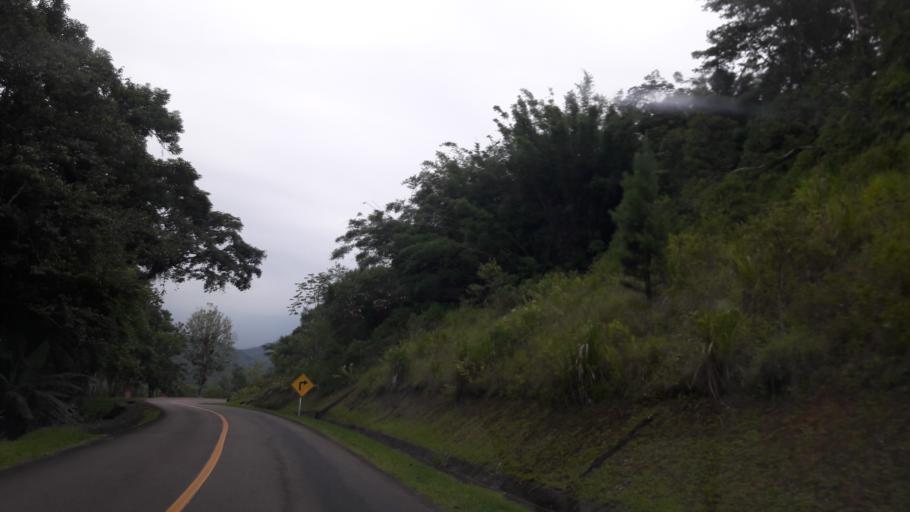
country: BR
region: Parana
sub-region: Antonina
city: Antonina
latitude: -25.4258
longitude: -48.8104
